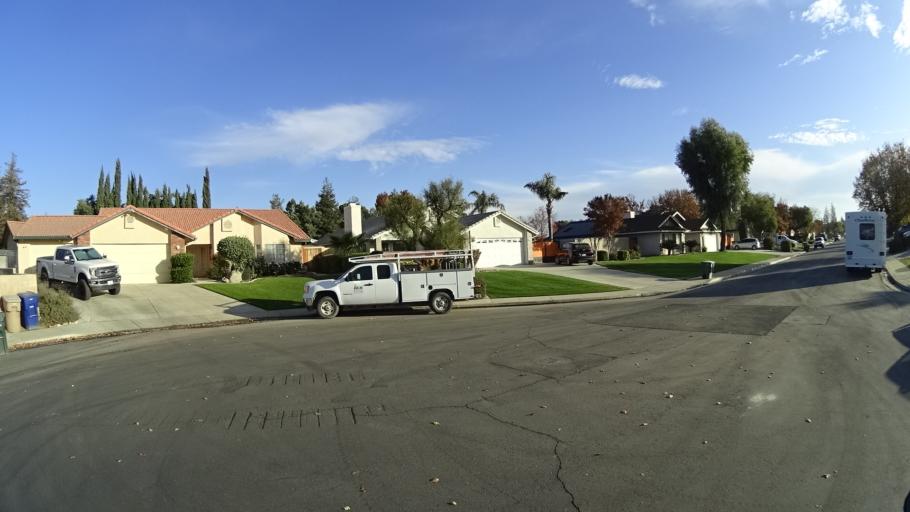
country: US
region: California
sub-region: Kern County
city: Rosedale
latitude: 35.3505
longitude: -119.1583
